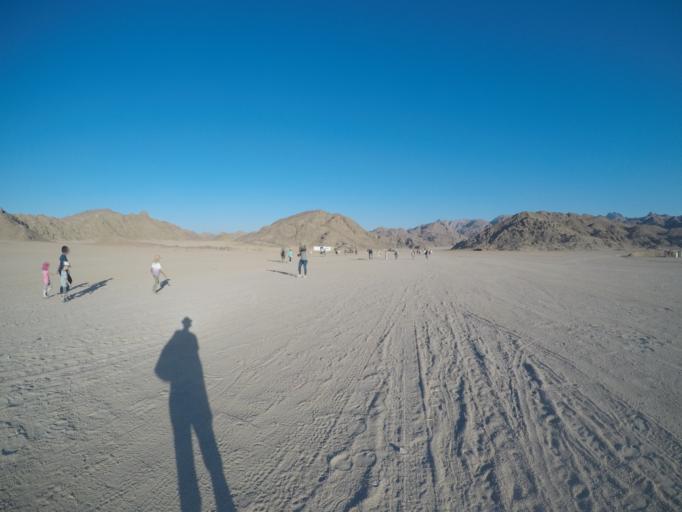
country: EG
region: Red Sea
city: El Gouna
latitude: 27.1519
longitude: 33.5437
